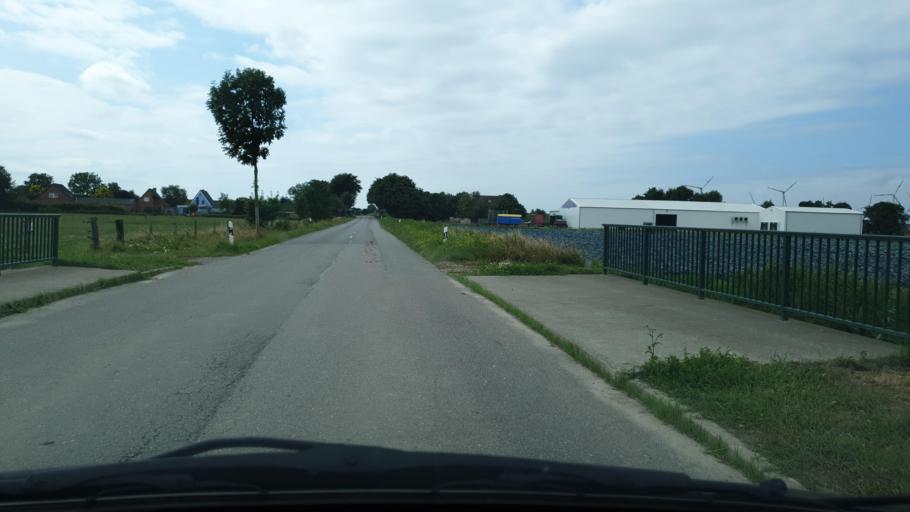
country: DE
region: Schleswig-Holstein
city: Kronprinzenkoog
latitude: 53.9481
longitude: 8.9501
